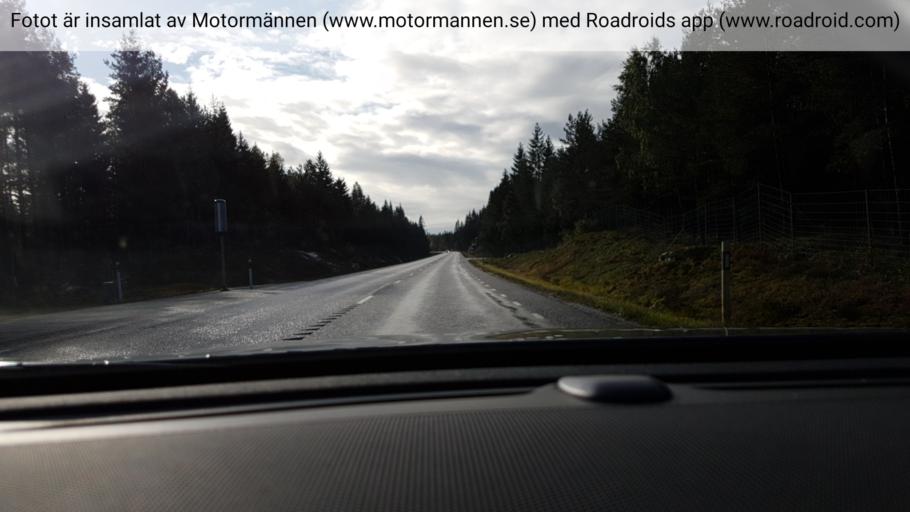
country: SE
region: Vaestra Goetaland
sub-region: Harryda Kommun
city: Hindas
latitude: 57.6636
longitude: 12.3681
